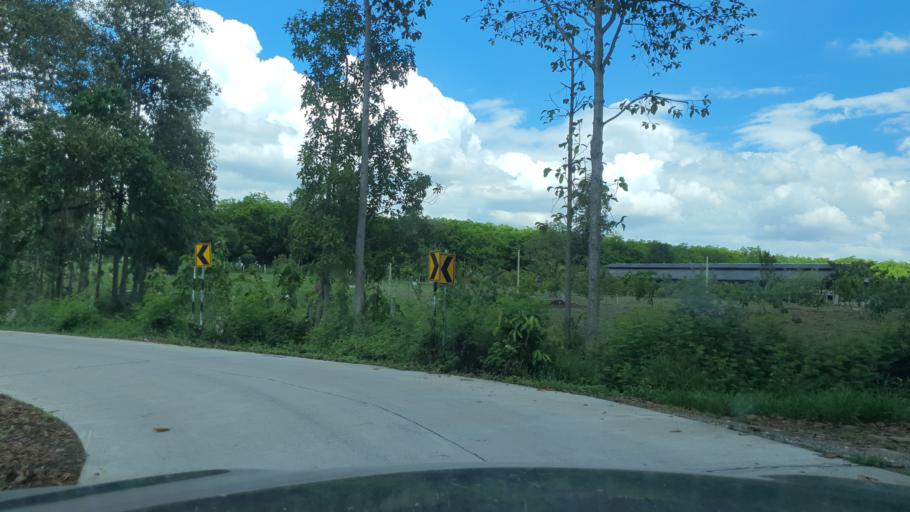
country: TH
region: Chiang Mai
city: San Sai
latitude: 18.9214
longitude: 99.0457
